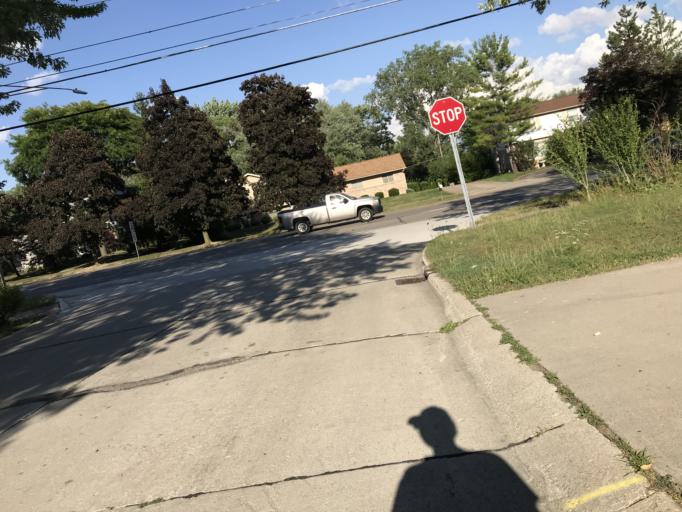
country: US
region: Michigan
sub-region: Oakland County
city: Farmington Hills
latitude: 42.4809
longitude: -83.3386
